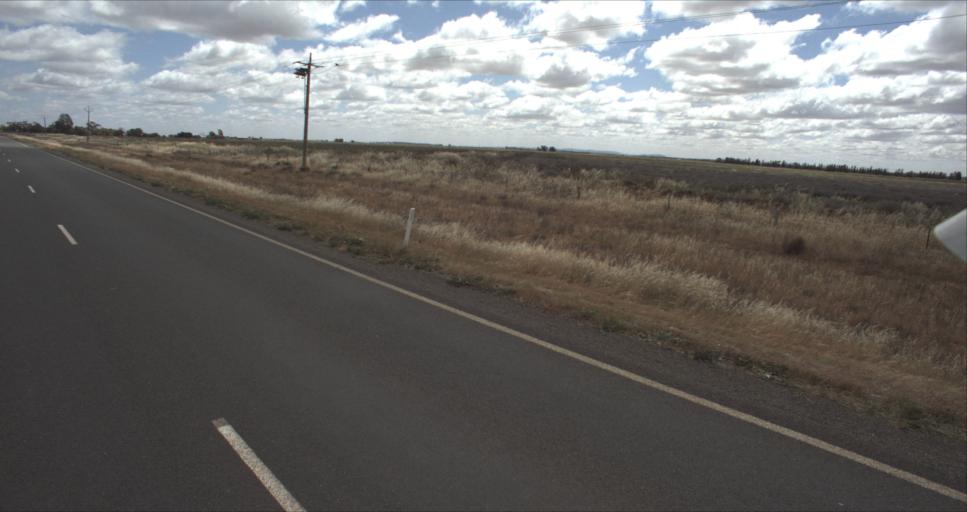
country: AU
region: New South Wales
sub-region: Murrumbidgee Shire
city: Darlington Point
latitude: -34.4912
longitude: 146.1650
